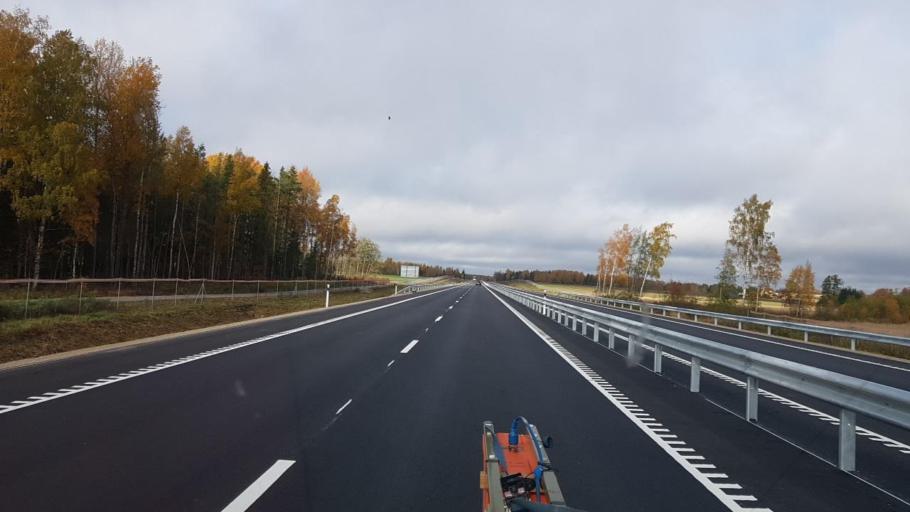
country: EE
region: Jaervamaa
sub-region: Paide linn
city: Paide
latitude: 58.9981
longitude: 25.5806
